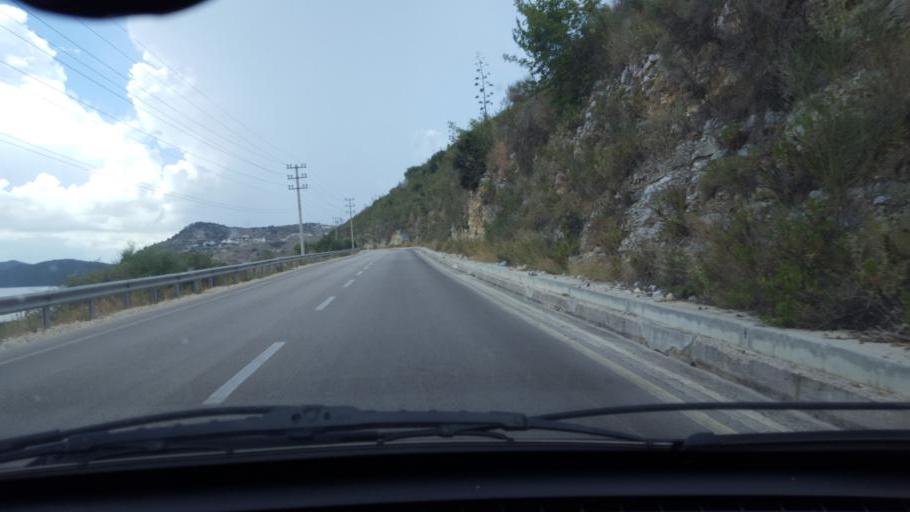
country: AL
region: Vlore
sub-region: Rrethi i Sarandes
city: Sarande
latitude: 39.8173
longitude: 20.0161
